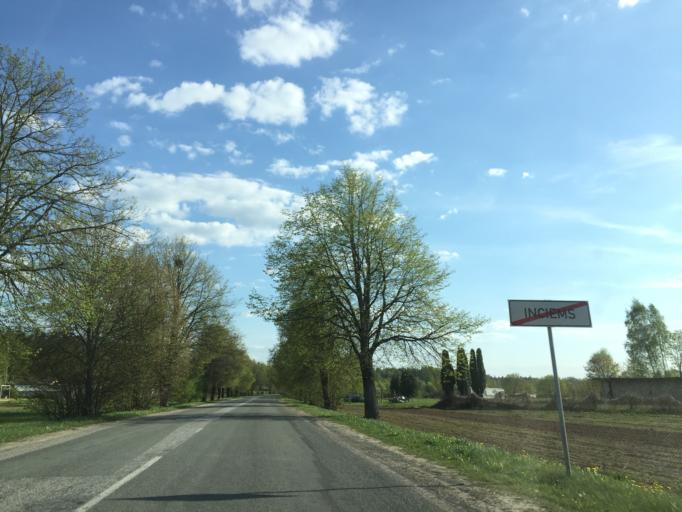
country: LV
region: Sigulda
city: Sigulda
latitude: 57.2536
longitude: 24.8741
